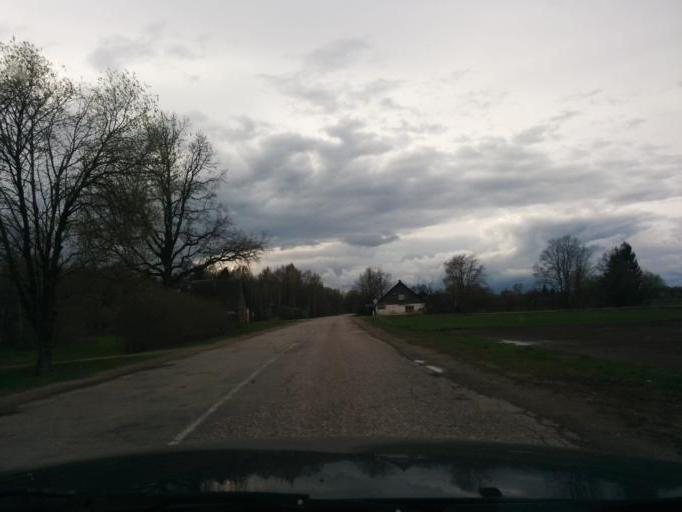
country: LV
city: Tervete
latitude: 56.4189
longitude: 23.5627
